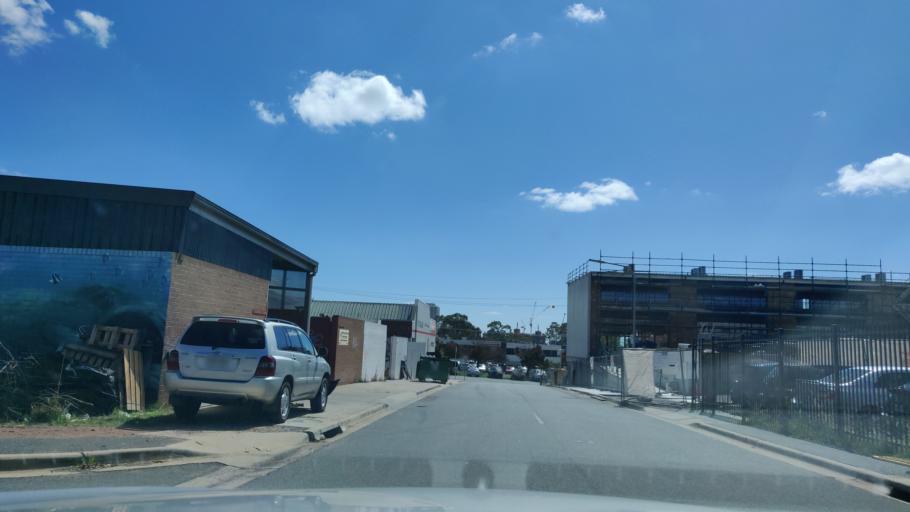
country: AU
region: Australian Capital Territory
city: Forrest
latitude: -35.3559
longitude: 149.0904
